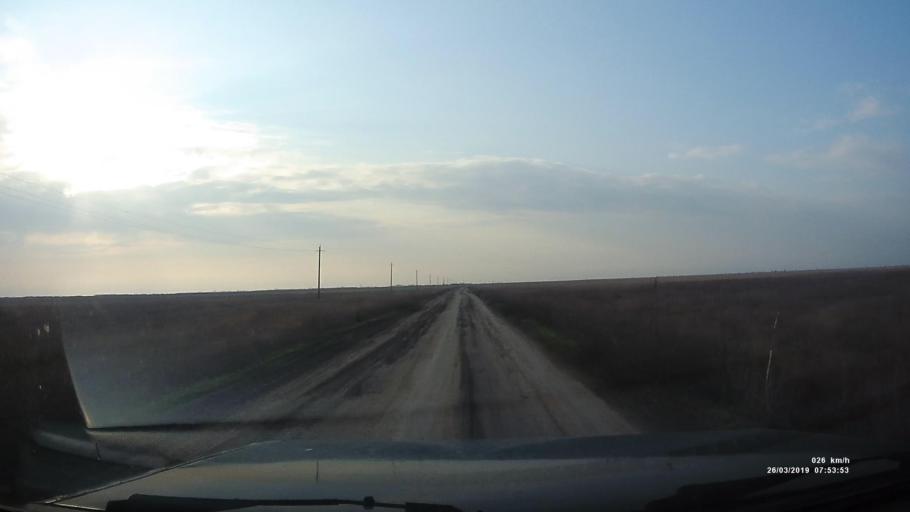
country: RU
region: Krasnodarskiy
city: Shabel'skoye
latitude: 47.1344
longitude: 38.5498
